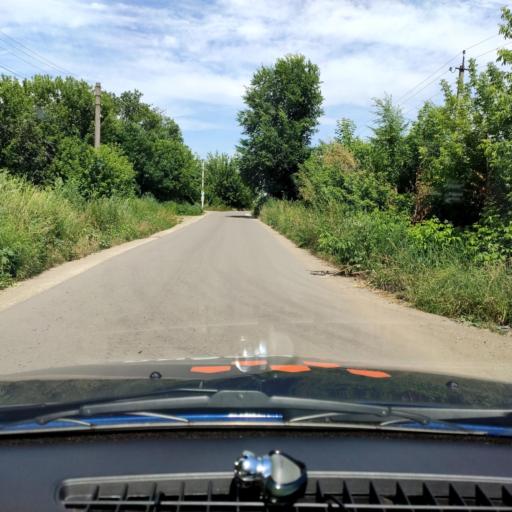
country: RU
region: Voronezj
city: Ramon'
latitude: 51.8287
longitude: 39.2669
